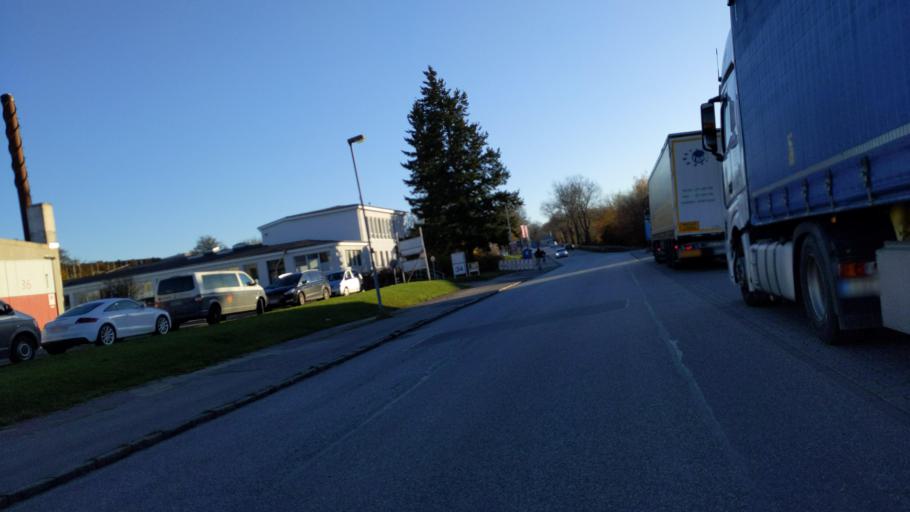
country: DE
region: Schleswig-Holstein
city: Bad Schwartau
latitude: 53.8931
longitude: 10.7072
